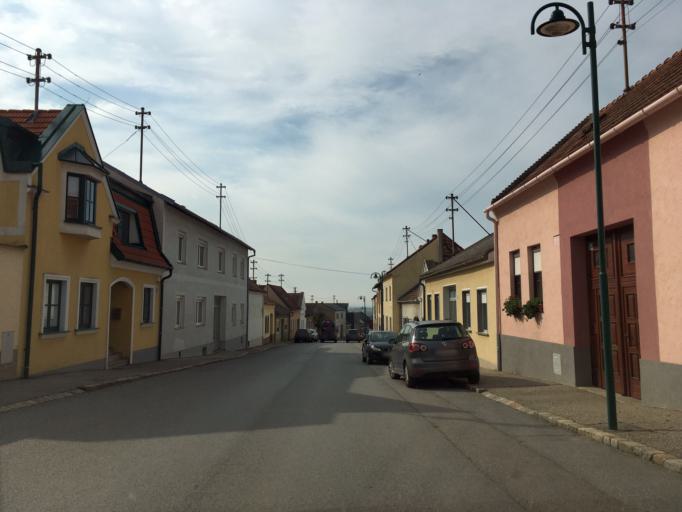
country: AT
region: Burgenland
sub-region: Politischer Bezirk Neusiedl am See
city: Jois
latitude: 47.9630
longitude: 16.7998
